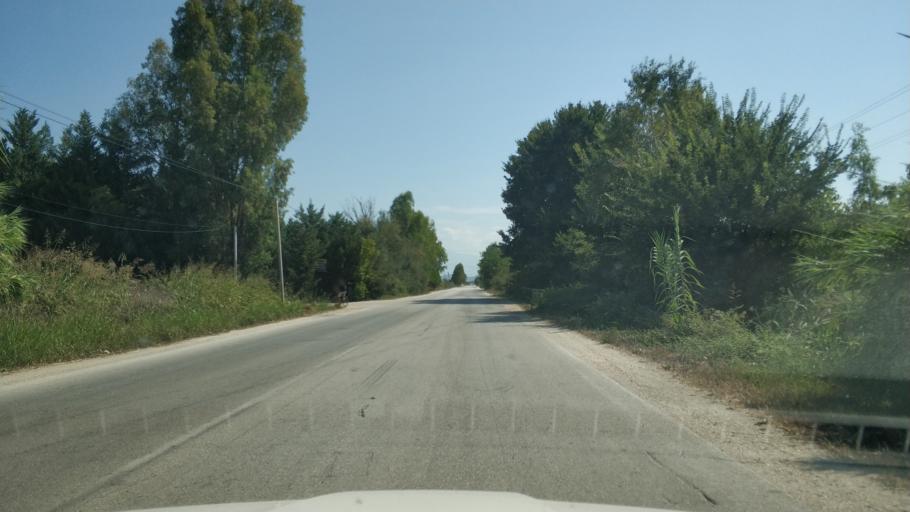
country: AL
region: Fier
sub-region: Rrethi i Lushnjes
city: Krutja e Poshtme
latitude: 40.8870
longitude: 19.6491
